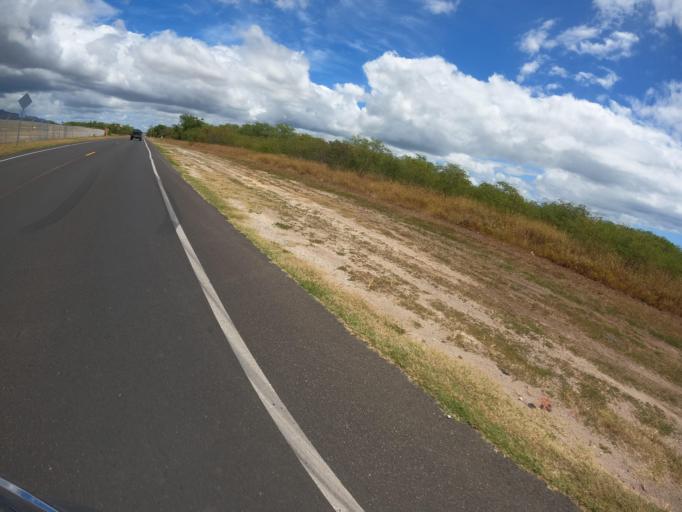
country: US
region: Hawaii
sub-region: Honolulu County
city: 'Ewa Villages
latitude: 21.3179
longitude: -158.0569
